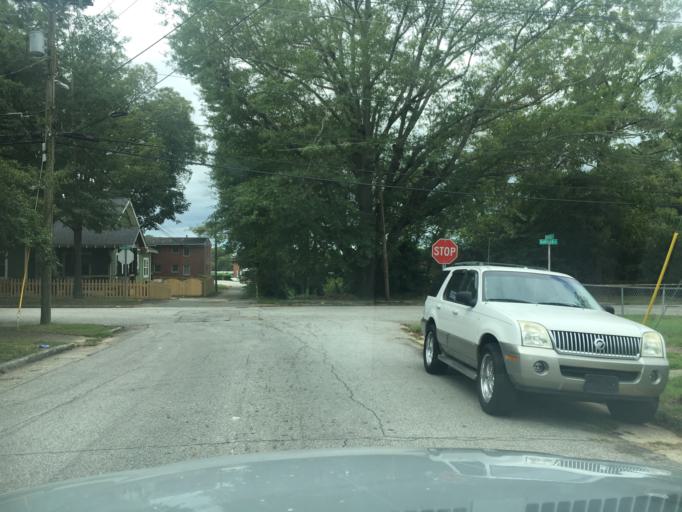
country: US
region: South Carolina
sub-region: Greenville County
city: Sans Souci
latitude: 34.8628
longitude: -82.4125
